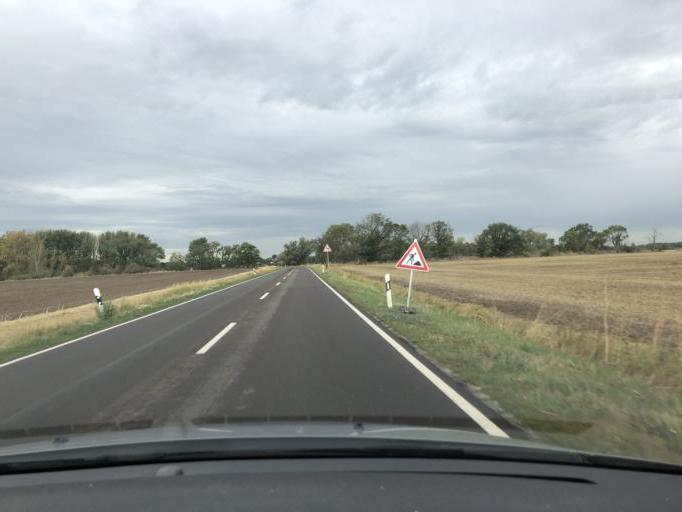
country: DE
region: Saxony-Anhalt
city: Calbe
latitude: 51.8875
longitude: 11.8083
